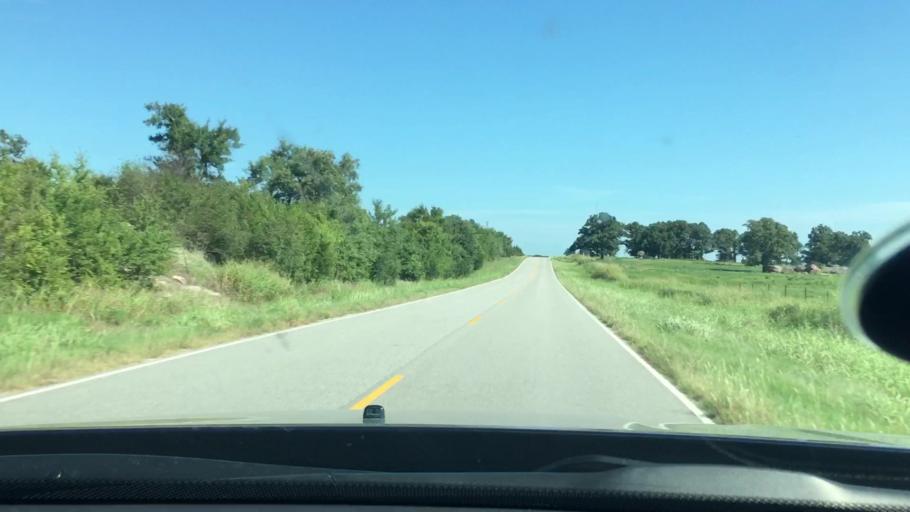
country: US
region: Oklahoma
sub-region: Johnston County
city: Tishomingo
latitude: 34.3483
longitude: -96.5488
